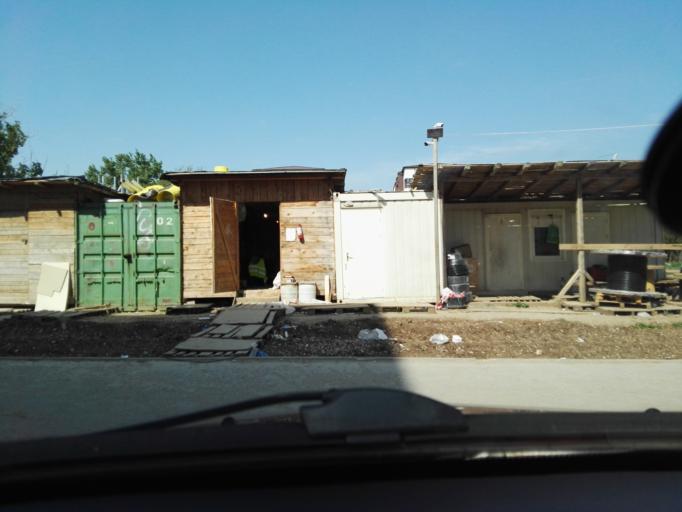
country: RO
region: Ilfov
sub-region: Comuna Popesti-Leordeni
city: Popesti-Leordeni
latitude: 44.3726
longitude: 26.1255
